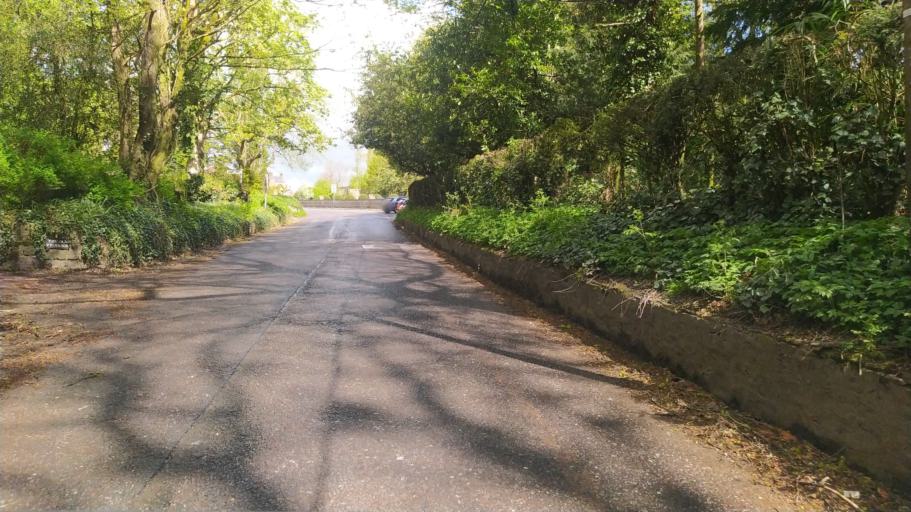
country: GB
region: England
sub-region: Wiltshire
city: Kilmington
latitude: 51.1460
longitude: -2.2825
